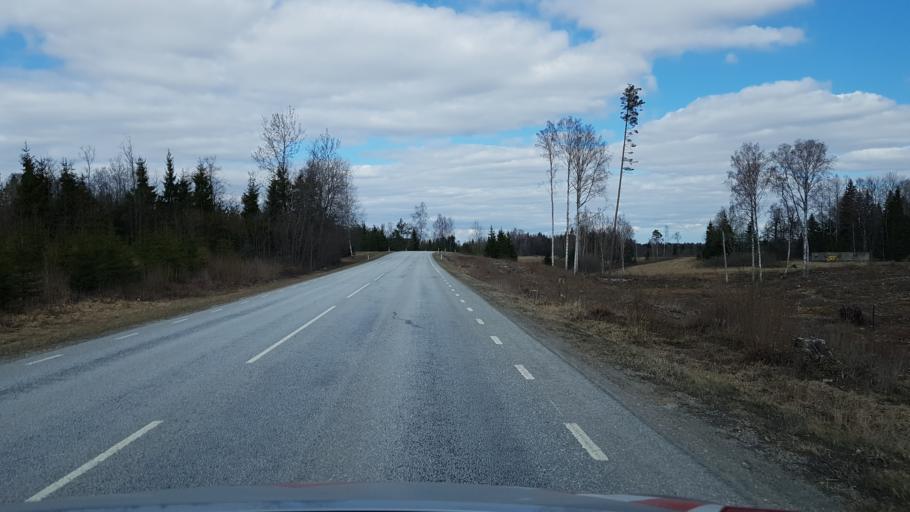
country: EE
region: Laeaene-Virumaa
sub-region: Rakke vald
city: Rakke
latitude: 58.9257
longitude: 26.2722
